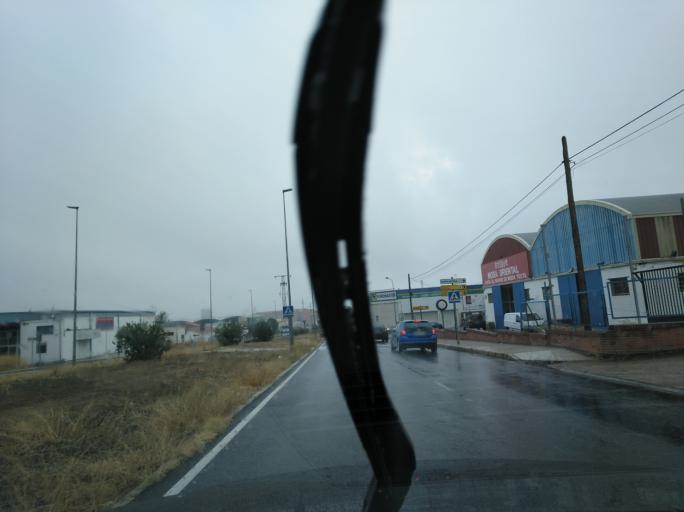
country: ES
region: Extremadura
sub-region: Provincia de Badajoz
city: Badajoz
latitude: 38.8945
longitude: -6.9922
